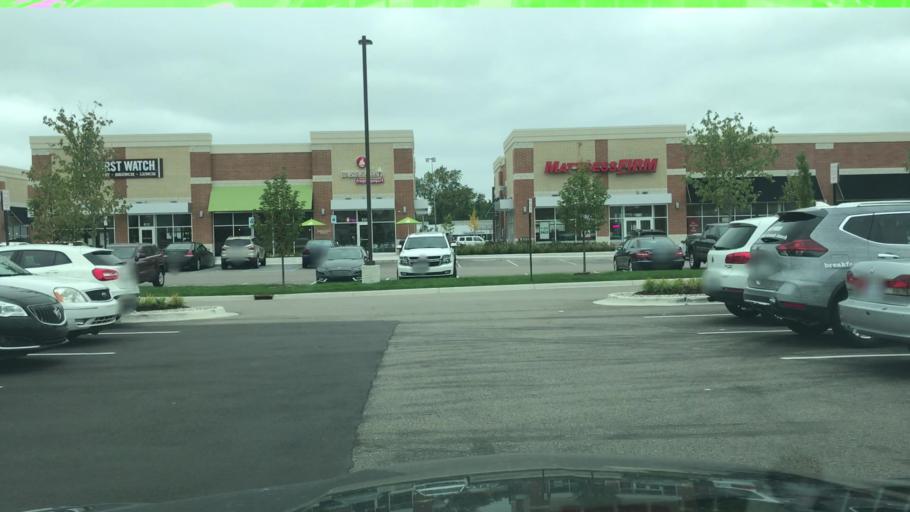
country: US
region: Michigan
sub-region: Oakland County
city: Clawson
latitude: 42.5618
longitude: -83.1314
